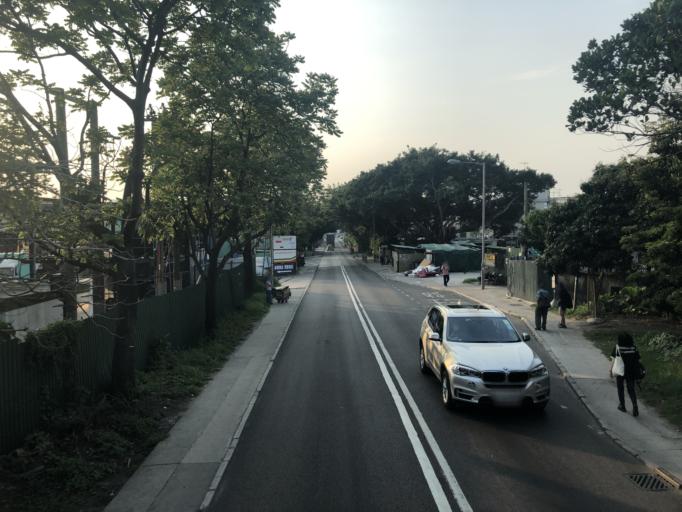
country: HK
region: Yuen Long
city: Yuen Long Kau Hui
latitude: 22.4639
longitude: 113.9868
